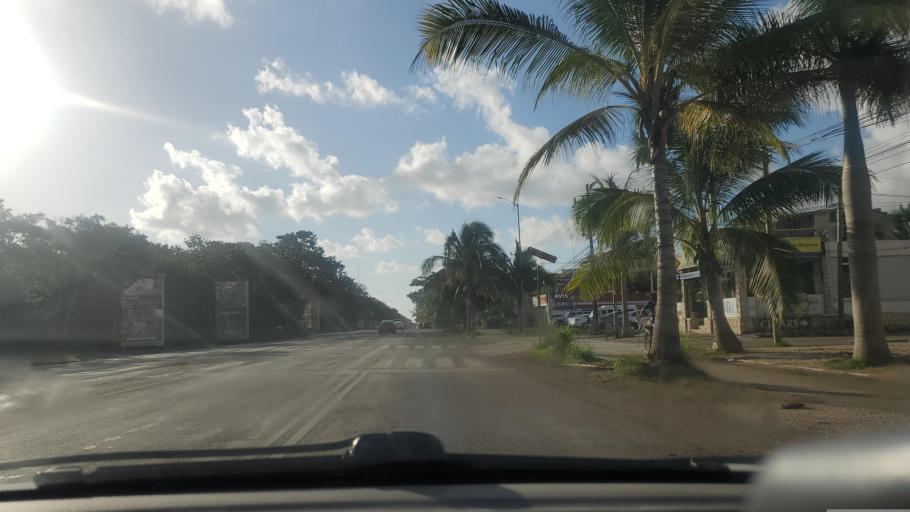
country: MX
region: Quintana Roo
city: Tulum
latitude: 20.2131
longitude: -87.4529
